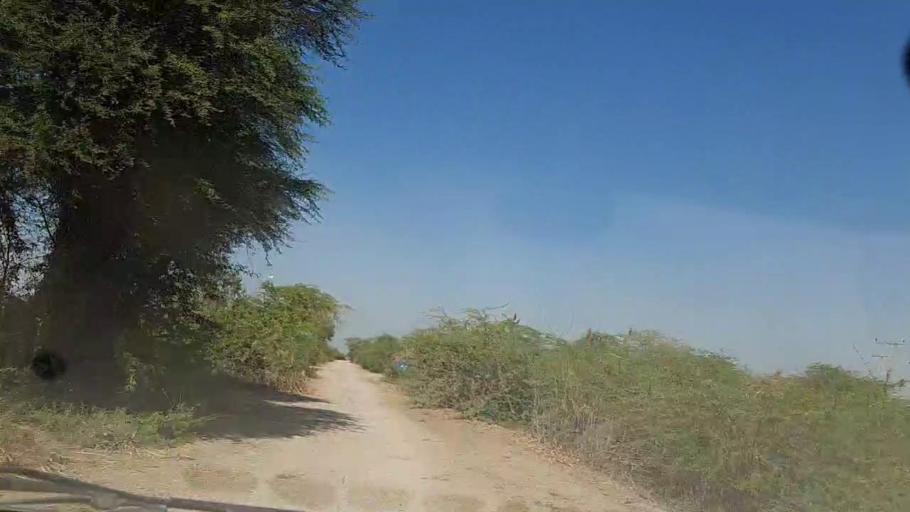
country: PK
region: Sindh
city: Mirpur Khas
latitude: 25.4235
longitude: 69.0420
